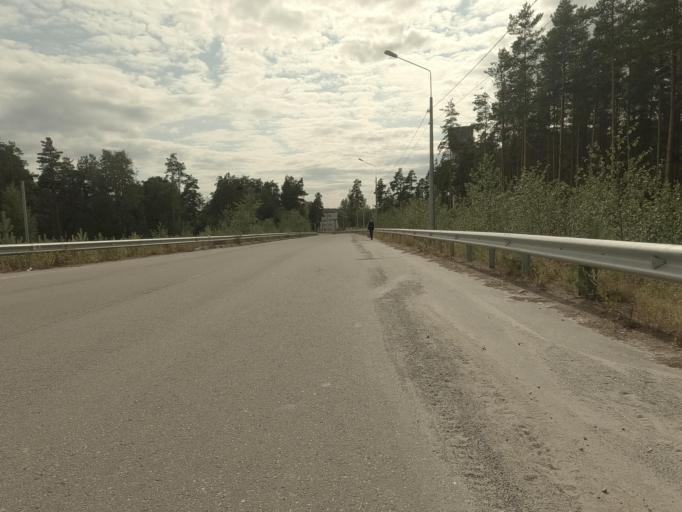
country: RU
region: Leningrad
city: Kamennogorsk
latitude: 60.9573
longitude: 29.1360
